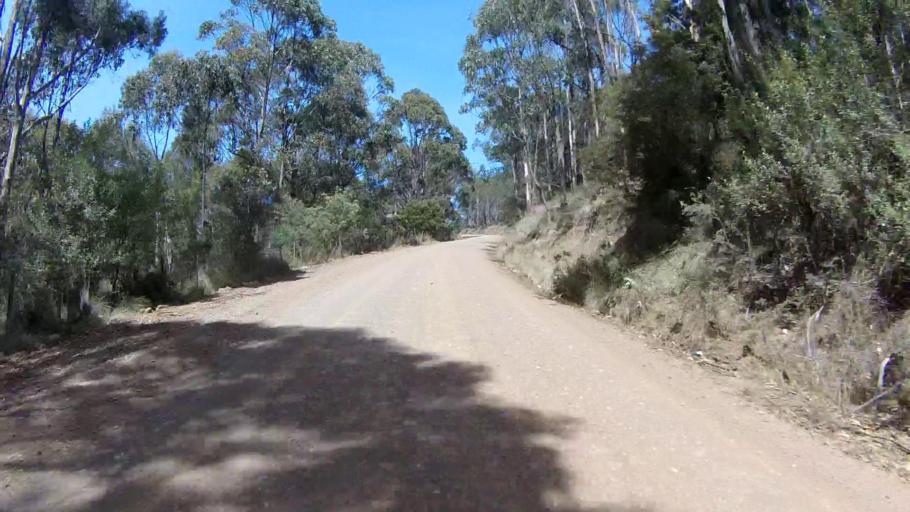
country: AU
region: Tasmania
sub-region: Sorell
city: Sorell
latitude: -42.6534
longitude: 147.7420
